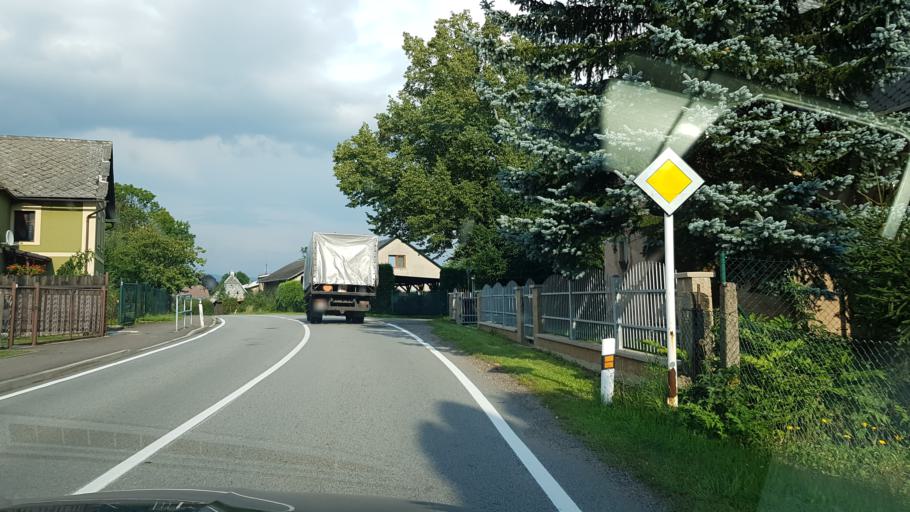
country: PL
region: Lower Silesian Voivodeship
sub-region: Powiat klodzki
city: Miedzylesie
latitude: 50.0960
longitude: 16.6593
